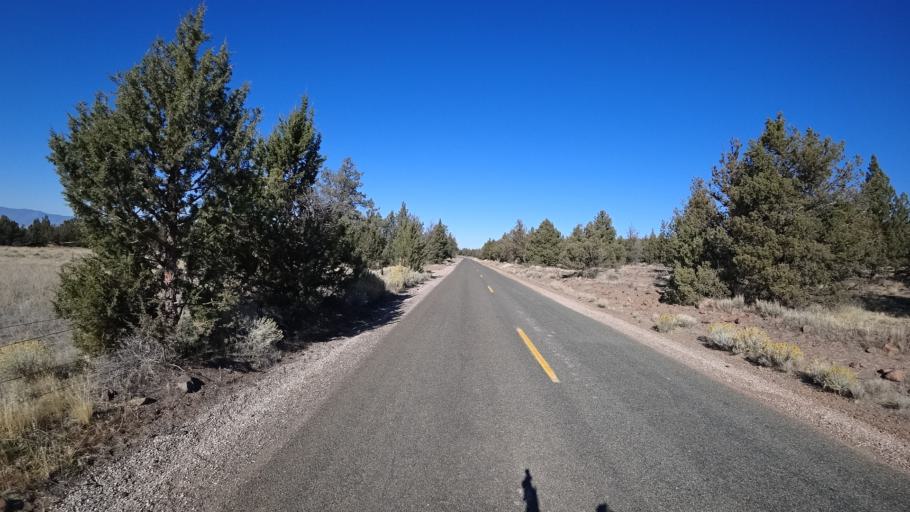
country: US
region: California
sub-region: Siskiyou County
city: Weed
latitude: 41.6087
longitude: -122.3105
